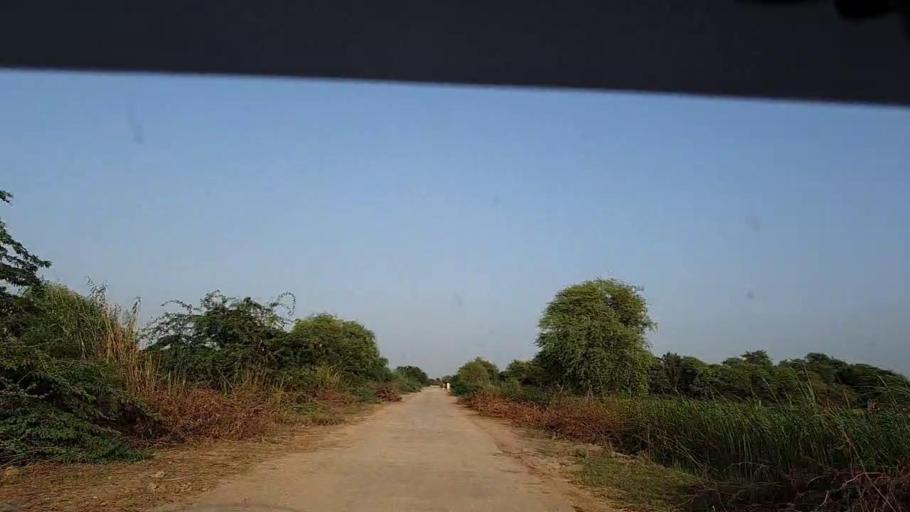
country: PK
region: Sindh
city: Kadhan
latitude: 24.5468
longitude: 68.9385
